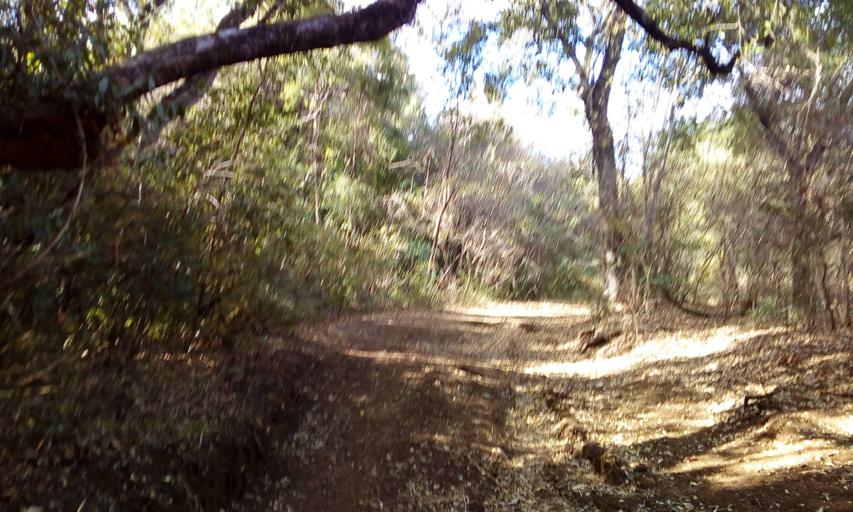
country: MG
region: Melaky
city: Mahabe
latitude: -16.3825
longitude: 45.3426
